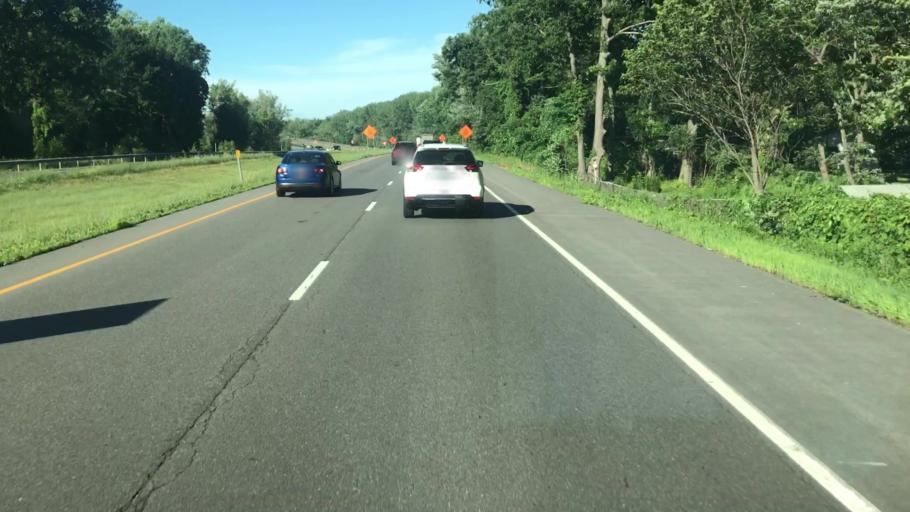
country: US
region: New York
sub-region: Onondaga County
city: Seneca Knolls
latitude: 43.1162
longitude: -76.2574
